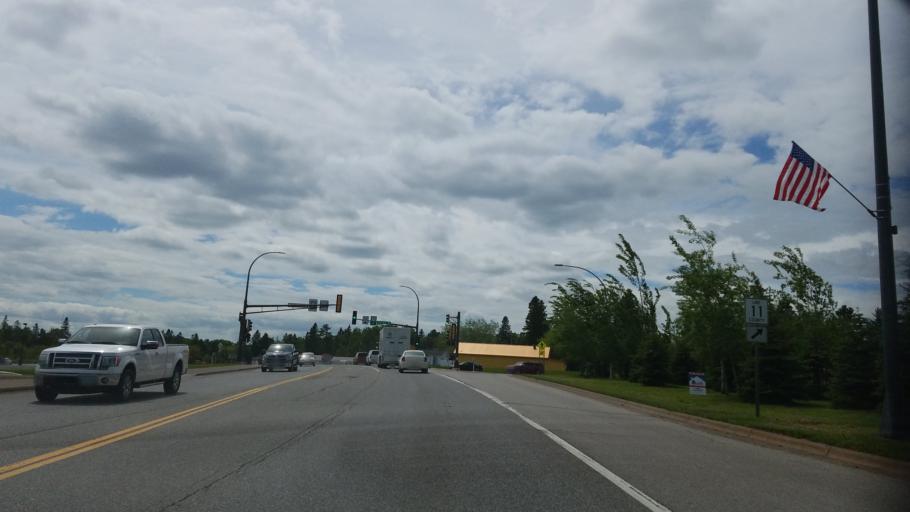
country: US
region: Minnesota
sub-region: Lake County
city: Two Harbors
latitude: 47.0255
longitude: -91.6890
